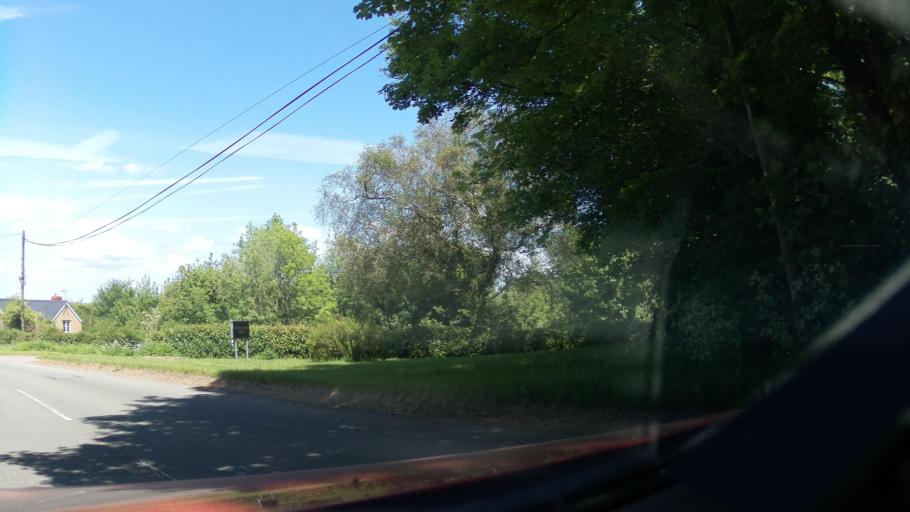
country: GB
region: Wales
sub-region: Monmouthshire
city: Tintern
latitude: 51.6978
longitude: -2.7527
